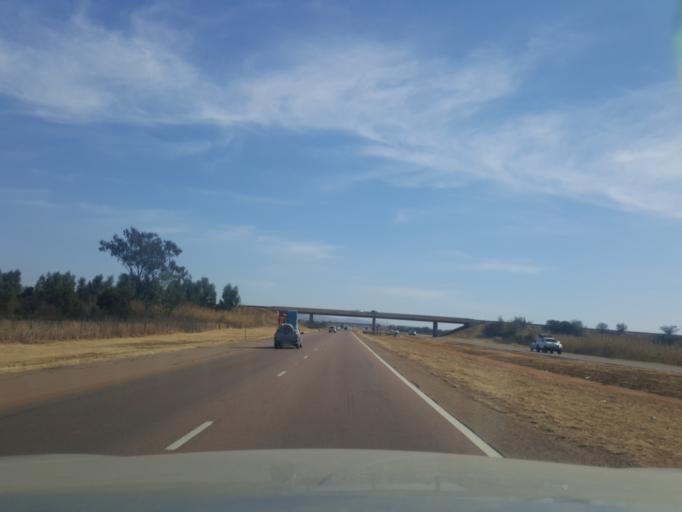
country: ZA
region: Gauteng
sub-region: City of Tshwane Metropolitan Municipality
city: Pretoria
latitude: -25.6410
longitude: 28.1819
